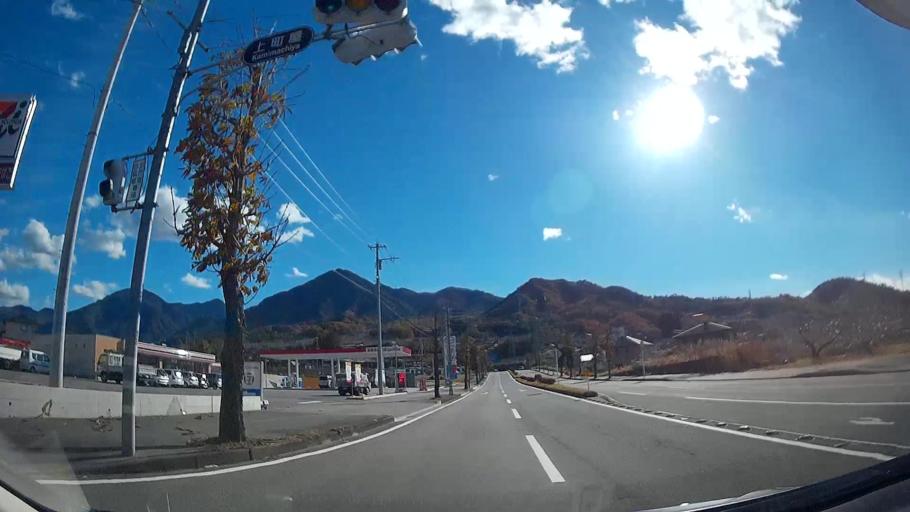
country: JP
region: Yamanashi
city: Isawa
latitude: 35.6187
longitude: 138.6941
